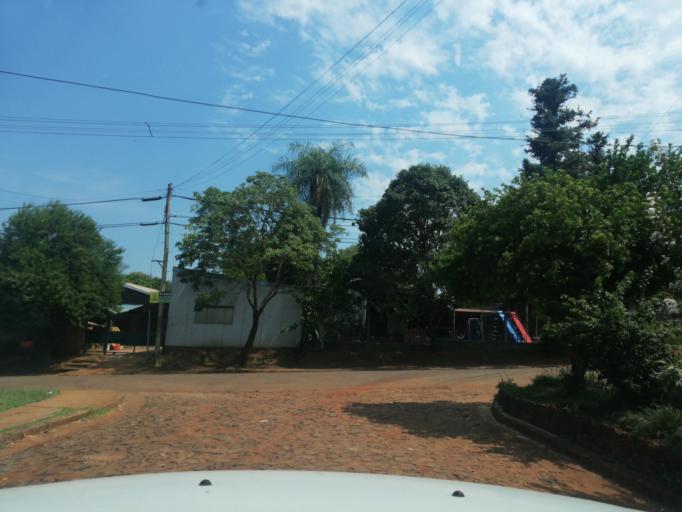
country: AR
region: Misiones
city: Garupa
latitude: -27.4396
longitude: -55.8839
